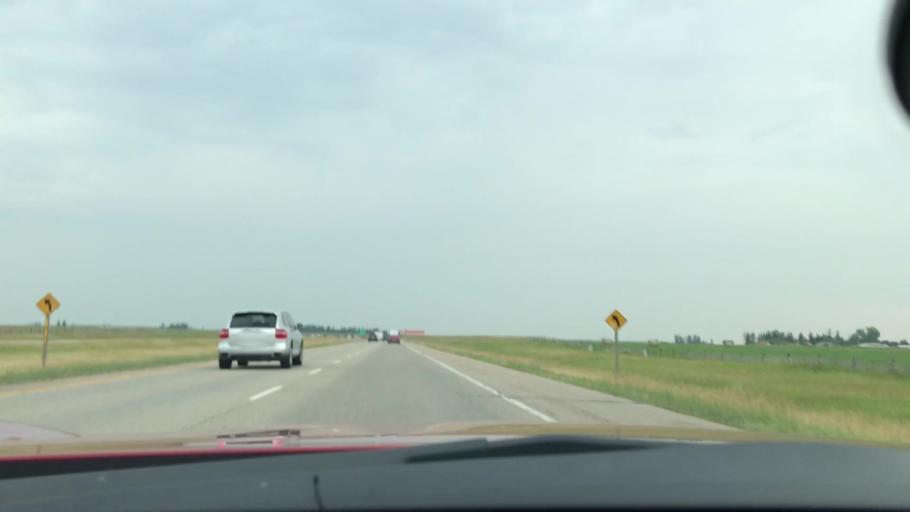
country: CA
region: Alberta
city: Leduc
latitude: 53.2044
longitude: -113.5940
